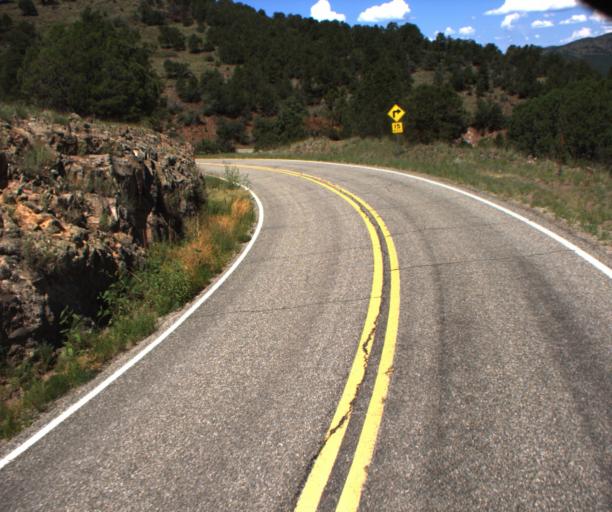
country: US
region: Arizona
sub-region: Greenlee County
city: Morenci
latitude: 33.3521
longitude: -109.3446
